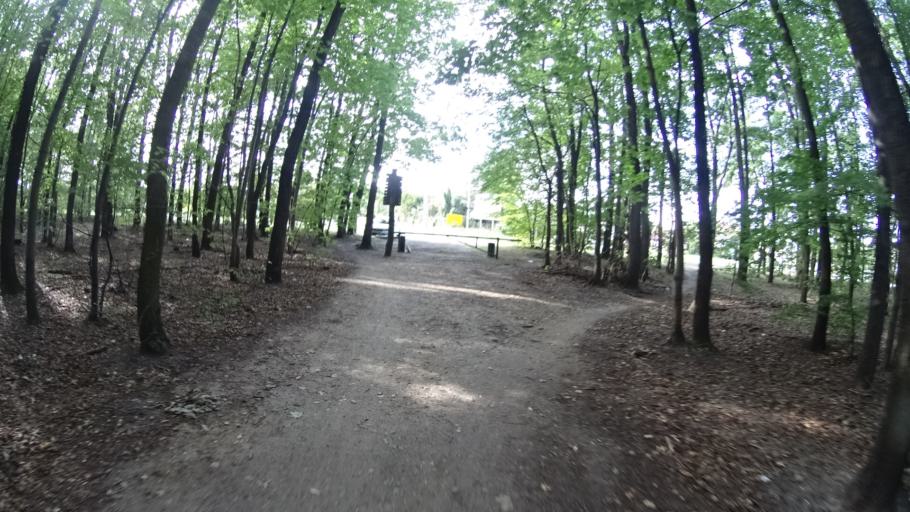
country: PL
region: Masovian Voivodeship
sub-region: Powiat warszawski zachodni
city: Babice
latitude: 52.2748
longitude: 20.8663
